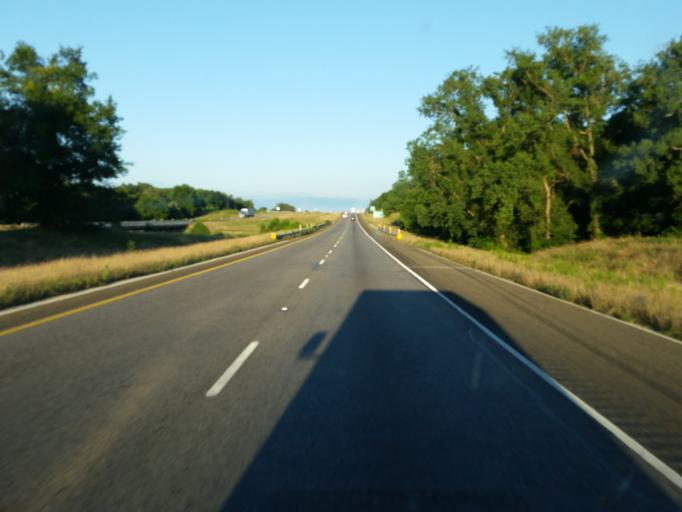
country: US
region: Texas
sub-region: Van Zandt County
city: Wills Point
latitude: 32.6614
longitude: -96.1184
